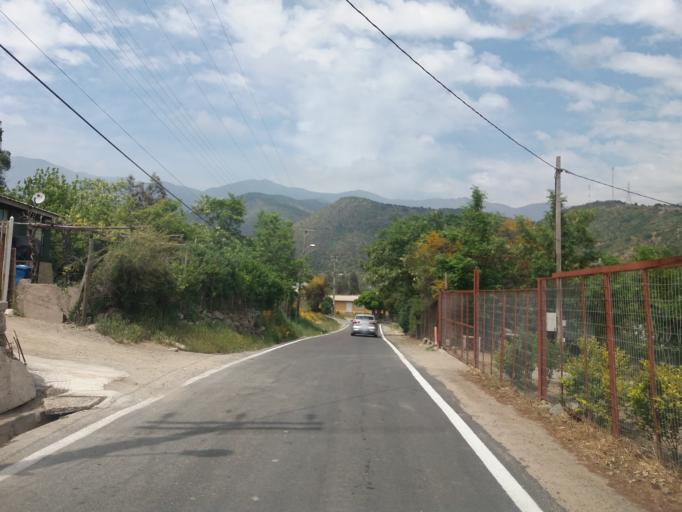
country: CL
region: Valparaiso
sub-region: Provincia de Marga Marga
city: Limache
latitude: -33.0471
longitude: -71.0994
